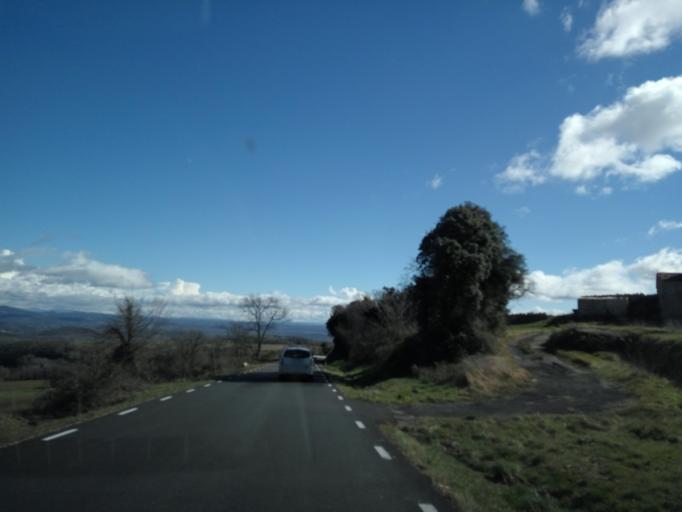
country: ES
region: Catalonia
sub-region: Provincia de Barcelona
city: Capolat
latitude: 42.0358
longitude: 1.7804
